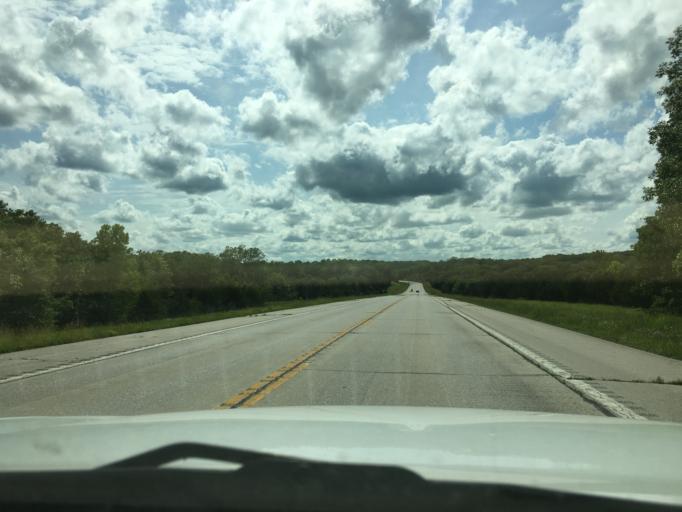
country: US
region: Missouri
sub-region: Franklin County
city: Gerald
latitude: 38.4236
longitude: -91.2698
